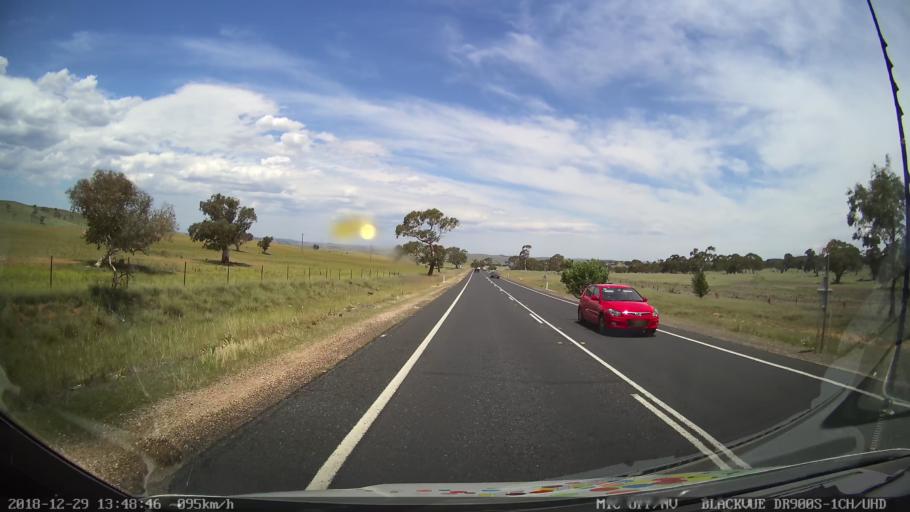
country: AU
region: New South Wales
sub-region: Cooma-Monaro
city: Cooma
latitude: -36.1447
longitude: 149.1492
